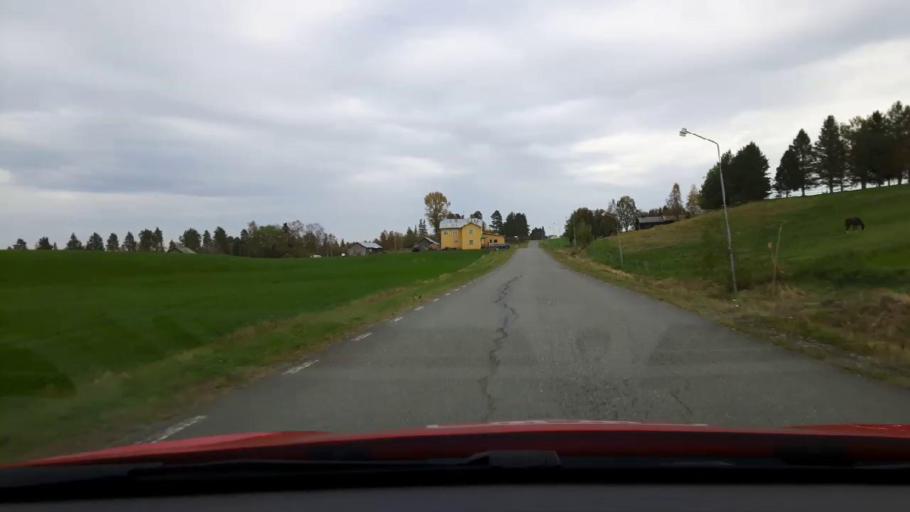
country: SE
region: Jaemtland
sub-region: Krokoms Kommun
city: Krokom
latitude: 63.2319
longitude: 14.1249
